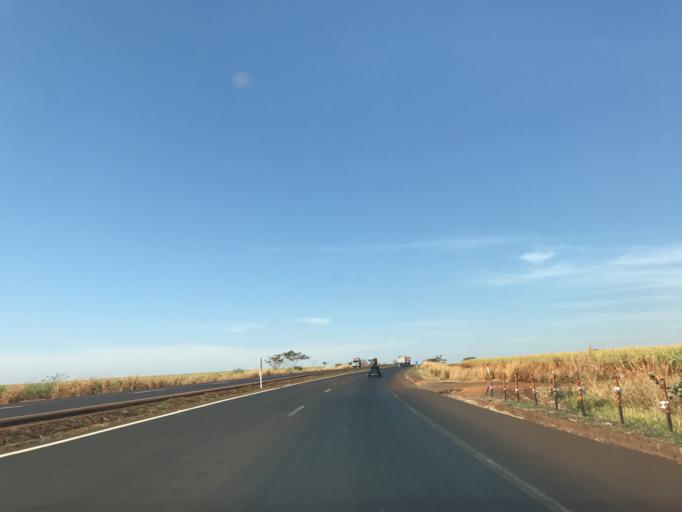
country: BR
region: Minas Gerais
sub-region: Centralina
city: Centralina
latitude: -18.5125
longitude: -49.1891
